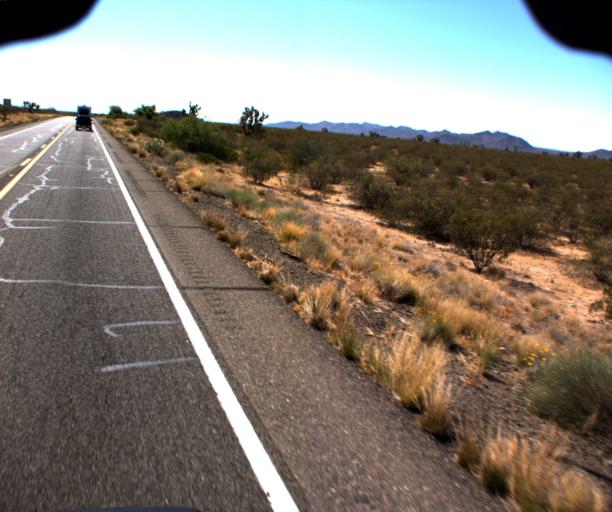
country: US
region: Arizona
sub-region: Yavapai County
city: Congress
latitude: 34.1817
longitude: -113.0382
